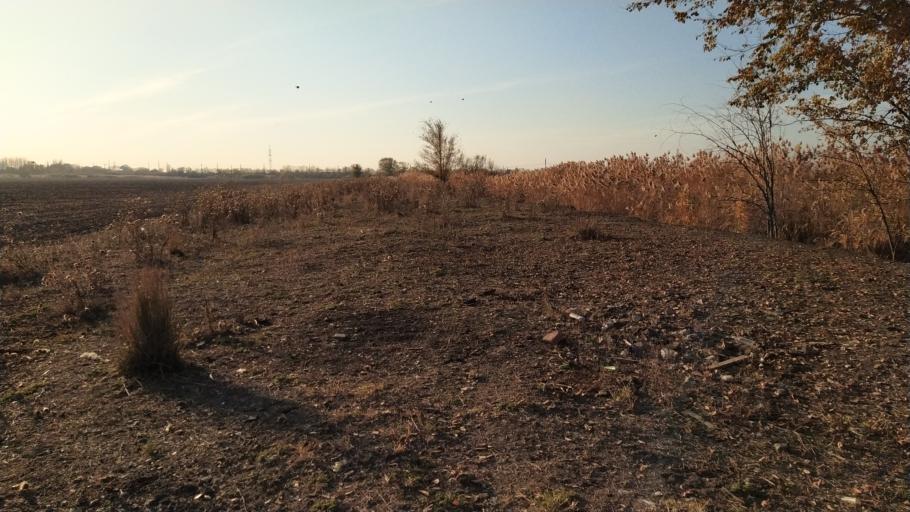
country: RU
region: Rostov
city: Bataysk
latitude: 47.1214
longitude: 39.7219
